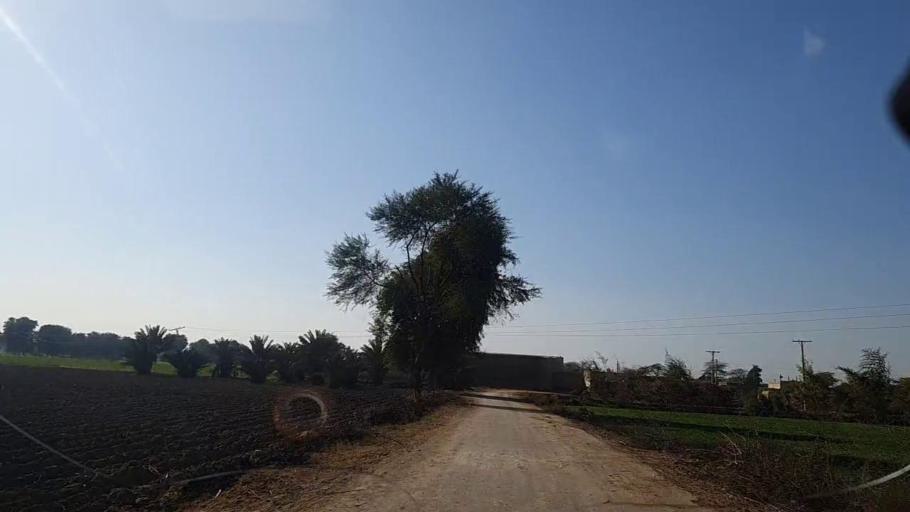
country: PK
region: Sindh
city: Khanpur
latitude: 27.7785
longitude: 69.3572
